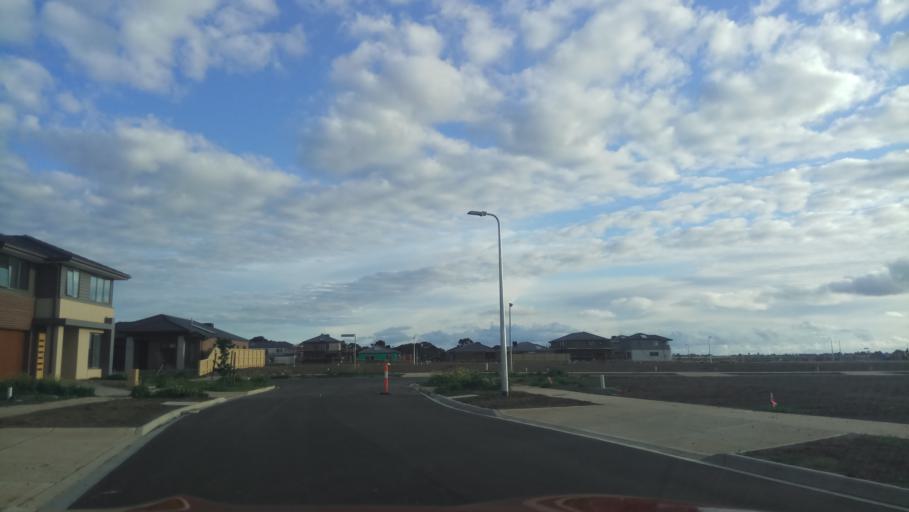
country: AU
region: Victoria
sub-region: Wyndham
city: Point Cook
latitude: -37.9118
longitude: 144.7493
